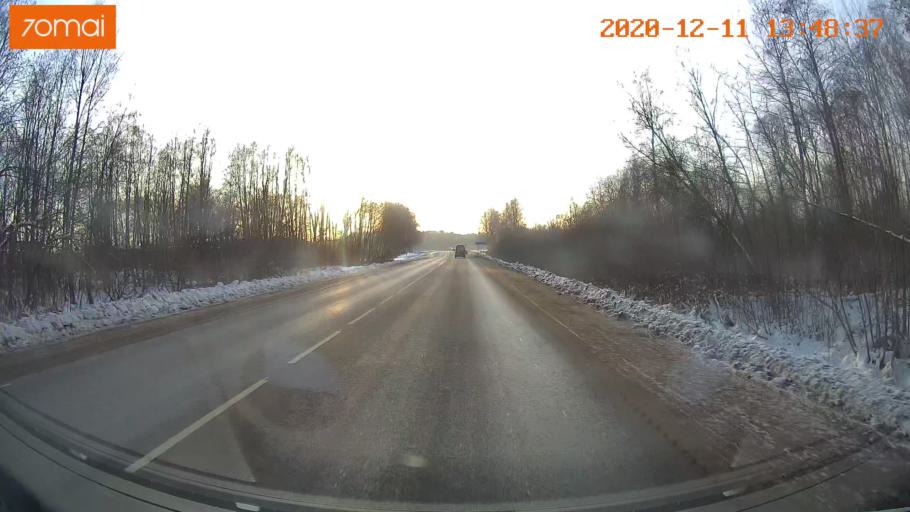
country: RU
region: Kostroma
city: Oktyabr'skiy
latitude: 57.8097
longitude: 41.0116
